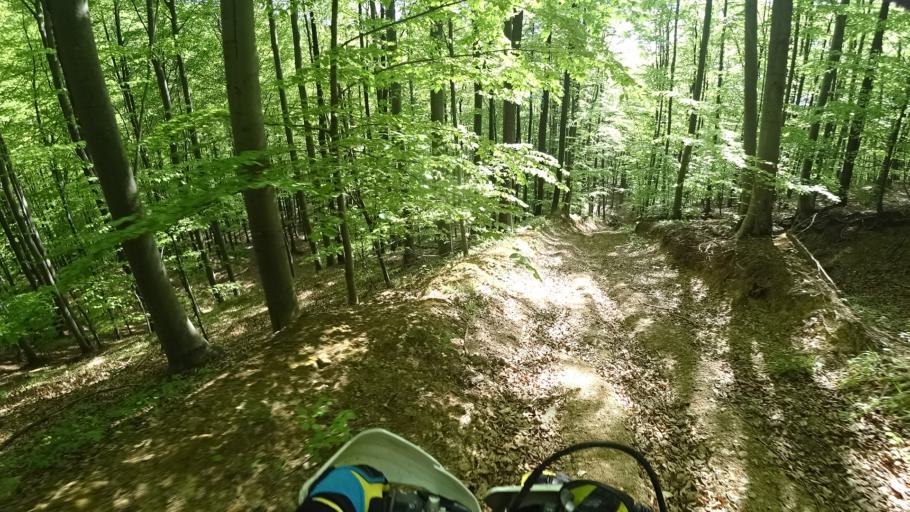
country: HR
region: Zagrebacka
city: Jablanovec
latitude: 45.8929
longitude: 15.9039
